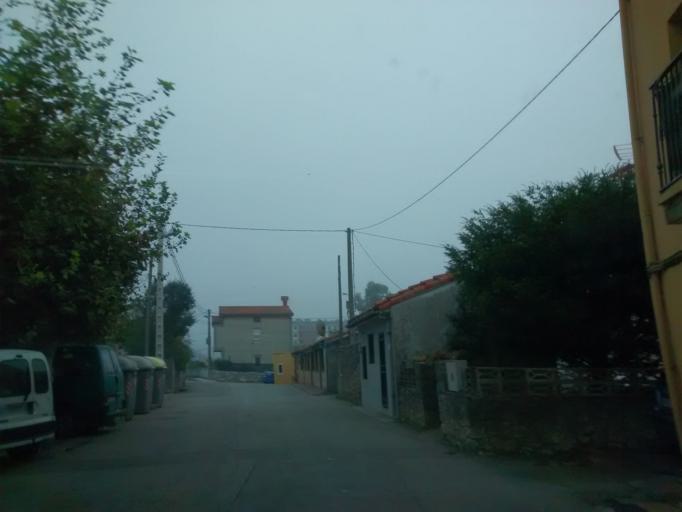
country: ES
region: Cantabria
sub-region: Provincia de Cantabria
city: Santander
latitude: 43.4709
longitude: -3.8299
